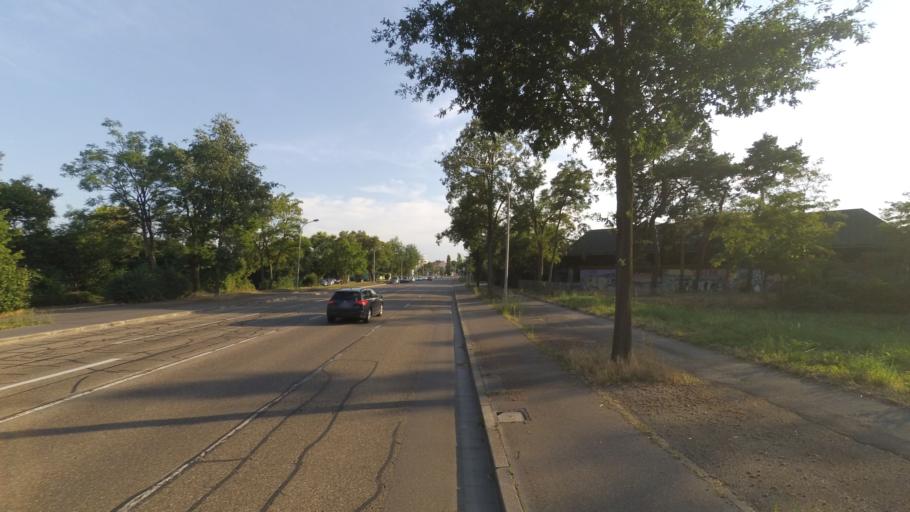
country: DE
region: Rheinland-Pfalz
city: Altrip
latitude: 49.4421
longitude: 8.5260
